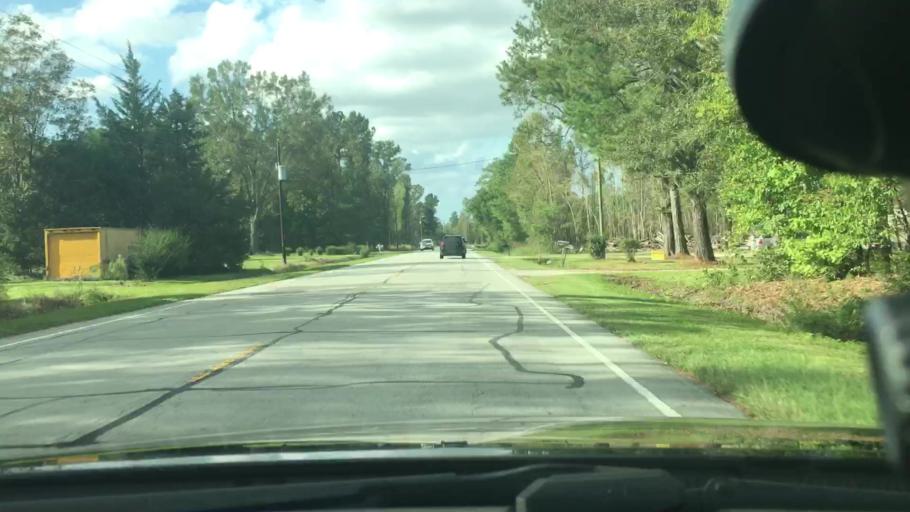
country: US
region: North Carolina
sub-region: Craven County
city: Vanceboro
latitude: 35.3258
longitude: -77.1684
